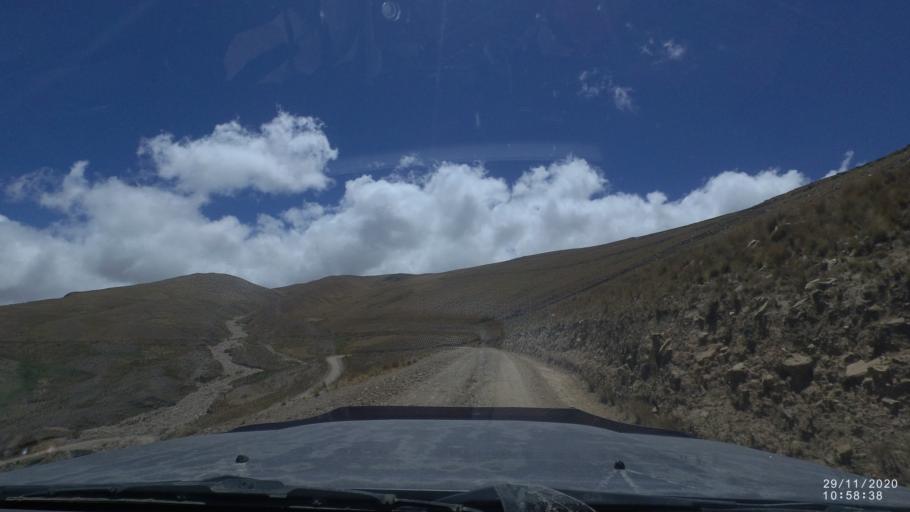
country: BO
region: Cochabamba
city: Cochabamba
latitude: -17.2088
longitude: -66.2289
